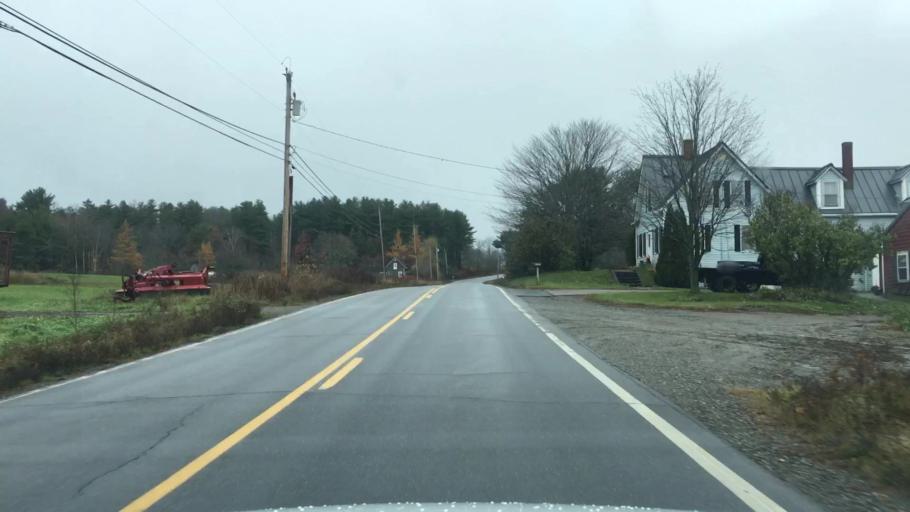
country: US
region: Maine
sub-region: Lincoln County
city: Jefferson
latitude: 44.1521
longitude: -69.4177
